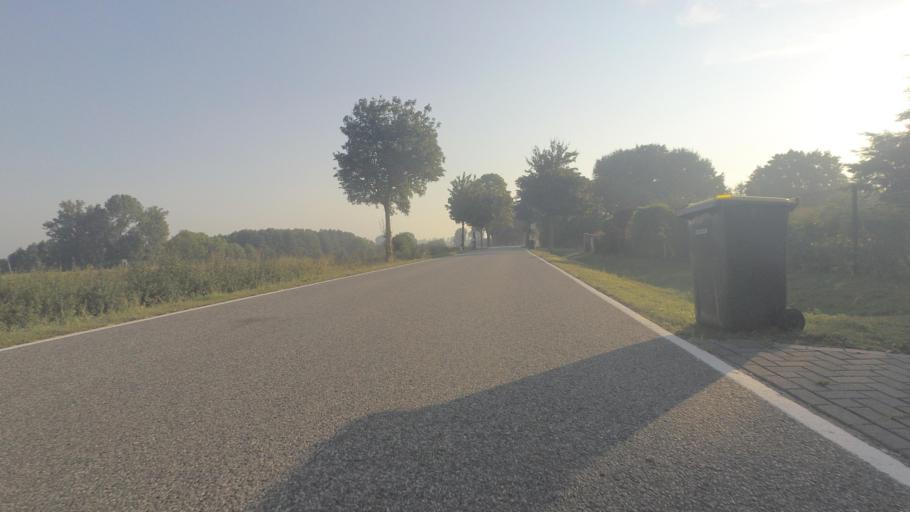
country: DE
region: Mecklenburg-Vorpommern
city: Demmin
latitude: 53.9208
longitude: 13.0708
